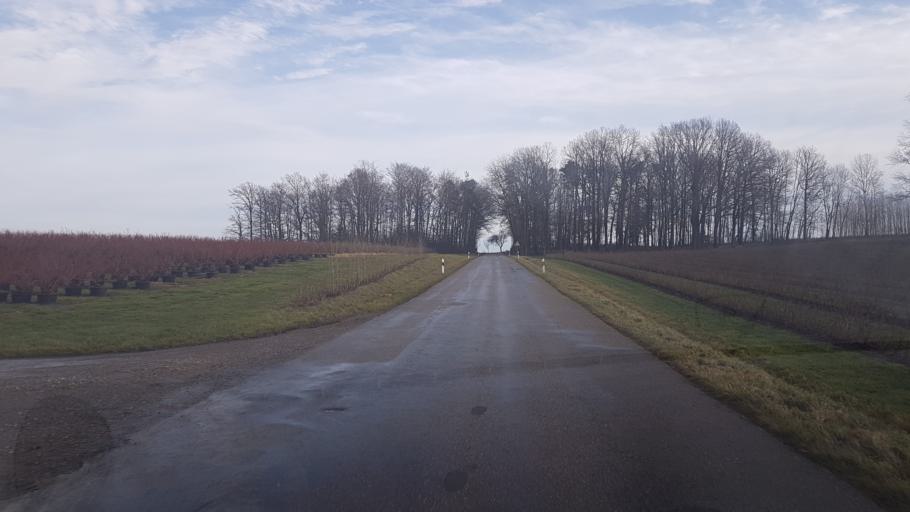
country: DE
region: Baden-Wuerttemberg
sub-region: Regierungsbezirk Stuttgart
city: Wallhausen
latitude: 49.2301
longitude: 10.0782
